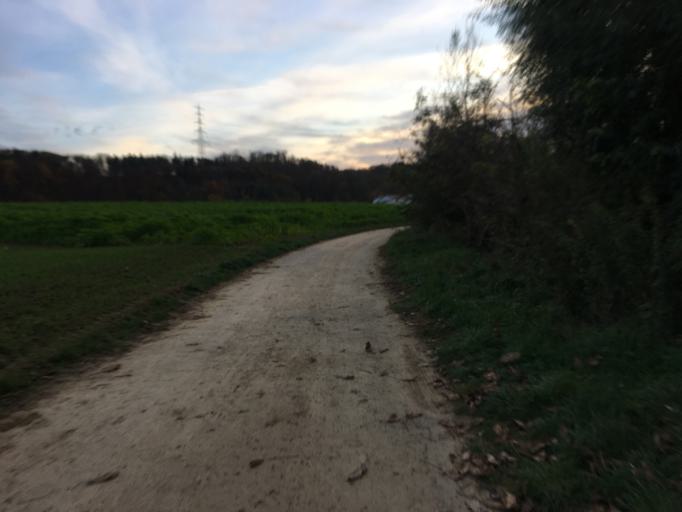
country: DE
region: Baden-Wuerttemberg
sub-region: Regierungsbezirk Stuttgart
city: Neckarwestheim
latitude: 49.0393
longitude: 9.1809
